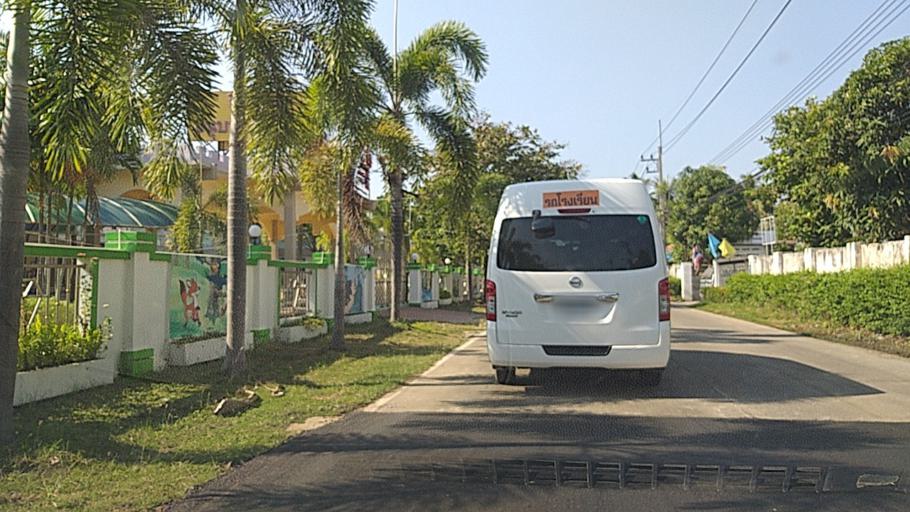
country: TH
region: Nakhon Pathom
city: Salaya
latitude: 13.8123
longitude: 100.3091
